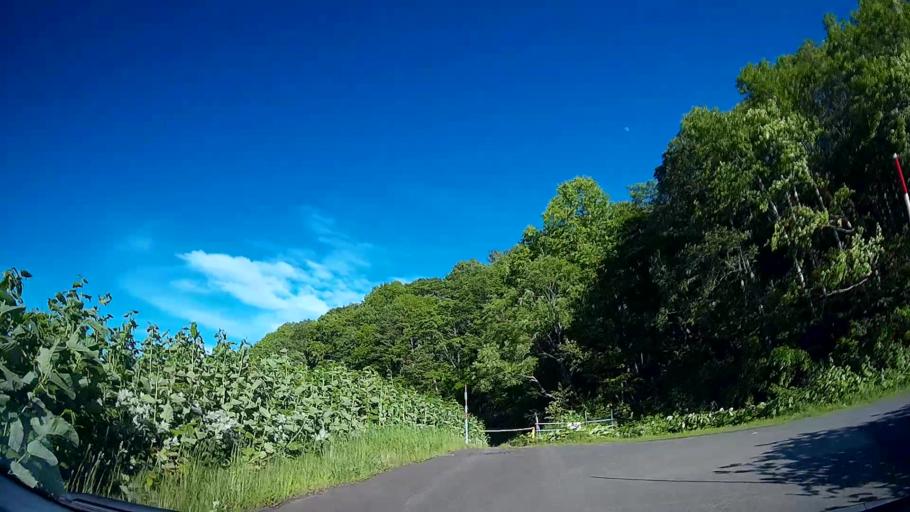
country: JP
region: Hokkaido
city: Otaru
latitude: 42.9806
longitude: 141.0441
